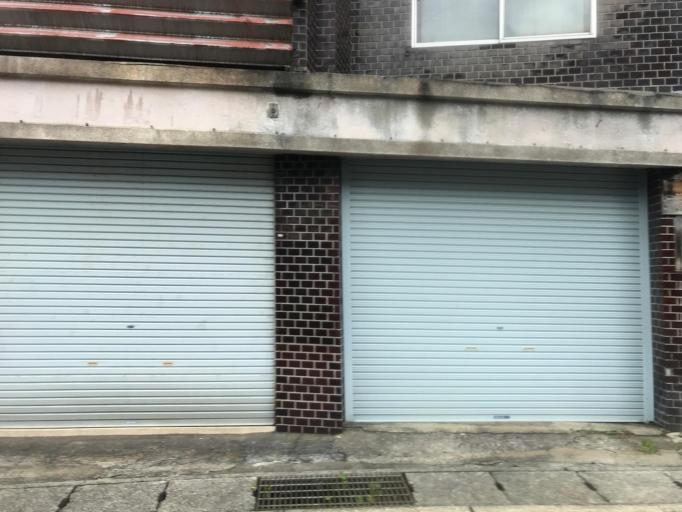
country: JP
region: Gunma
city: Numata
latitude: 36.7807
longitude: 138.9686
